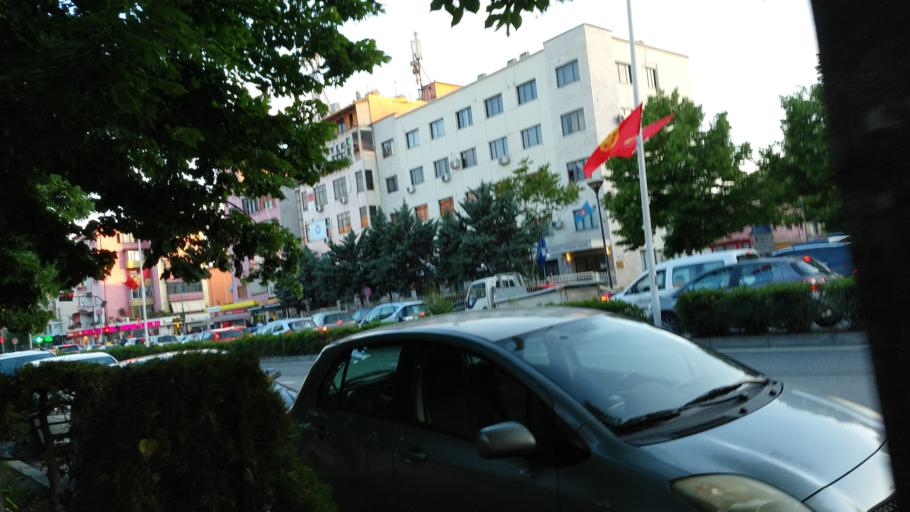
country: AL
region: Tirane
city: Tirana
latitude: 41.3267
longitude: 19.8033
